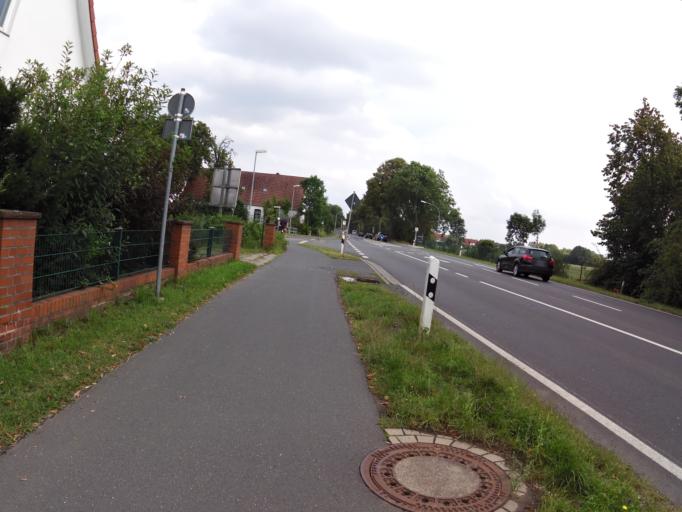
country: DE
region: Lower Saxony
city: Verden
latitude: 52.9213
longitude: 9.2078
